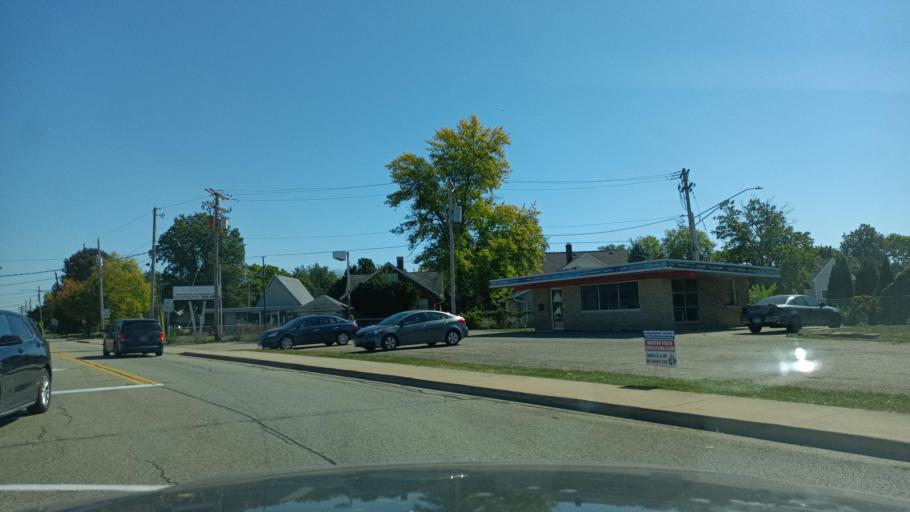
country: US
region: Illinois
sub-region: Tazewell County
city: Morton
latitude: 40.6128
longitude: -89.4597
